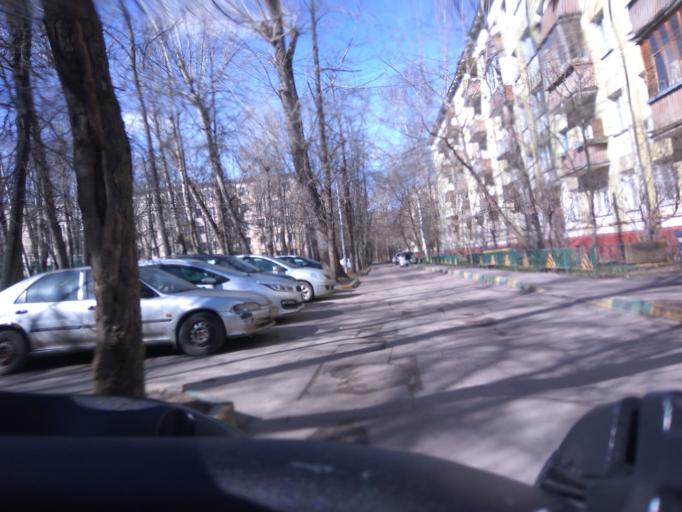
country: RU
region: Moskovskaya
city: Fili
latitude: 55.7332
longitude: 37.4839
